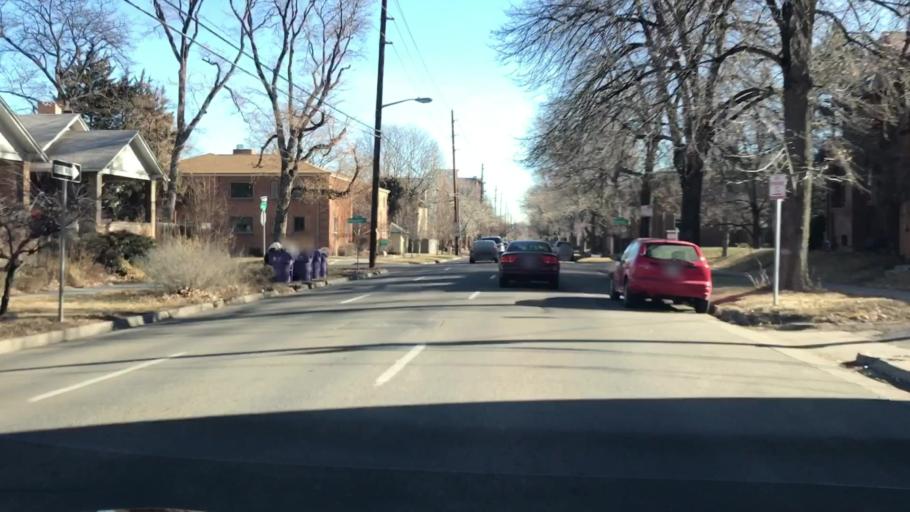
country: US
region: Colorado
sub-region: Denver County
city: Denver
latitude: 39.7384
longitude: -104.9523
